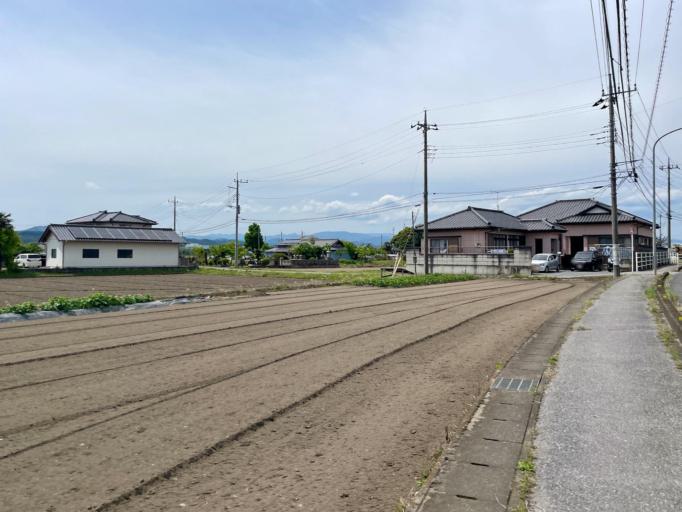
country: JP
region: Tochigi
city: Mibu
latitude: 36.4686
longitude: 139.7647
